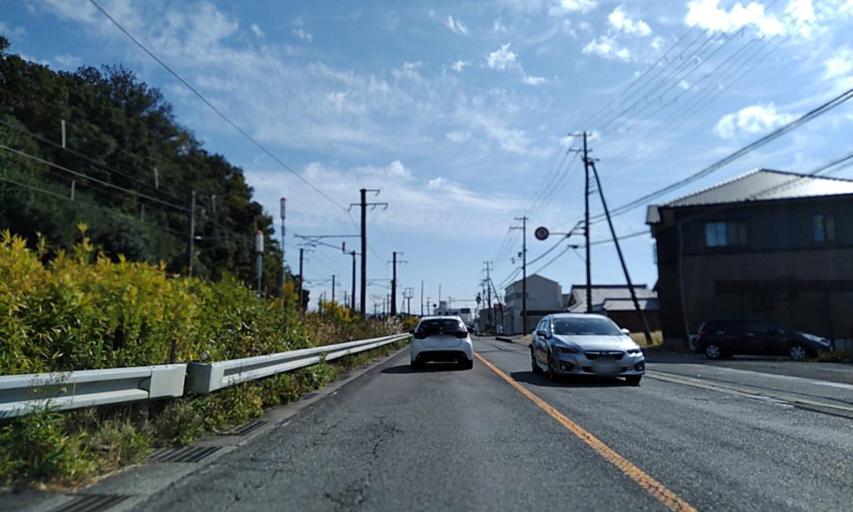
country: JP
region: Wakayama
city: Gobo
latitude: 33.9099
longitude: 135.1500
